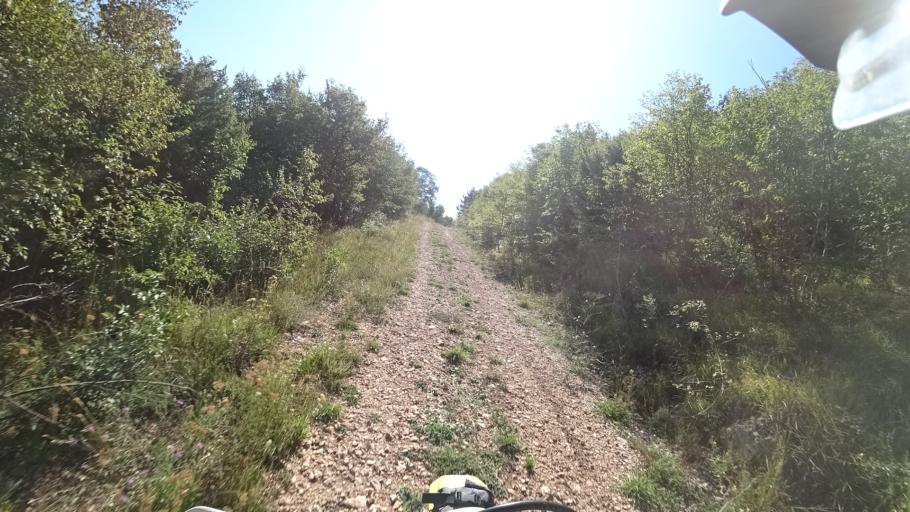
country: HR
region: Sibensko-Kniniska
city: Drnis
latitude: 43.9325
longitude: 16.1701
